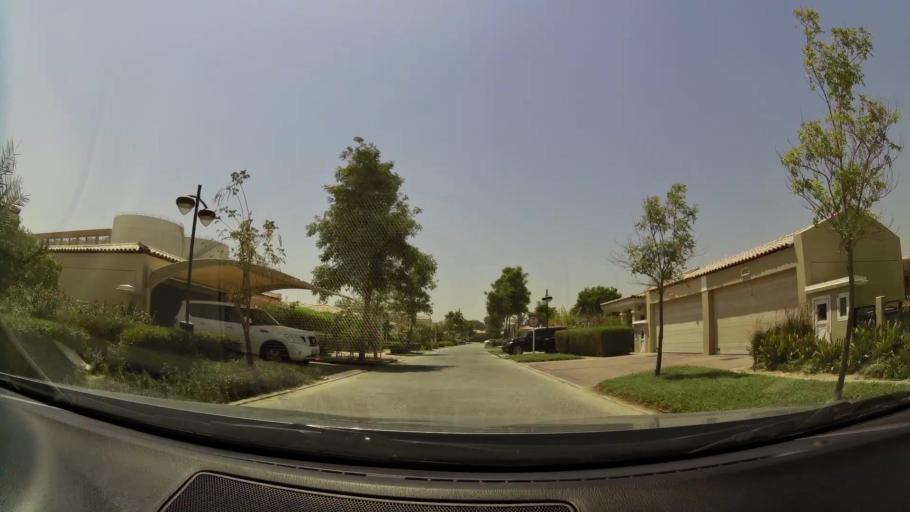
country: AE
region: Dubai
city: Dubai
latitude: 24.9910
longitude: 55.1650
